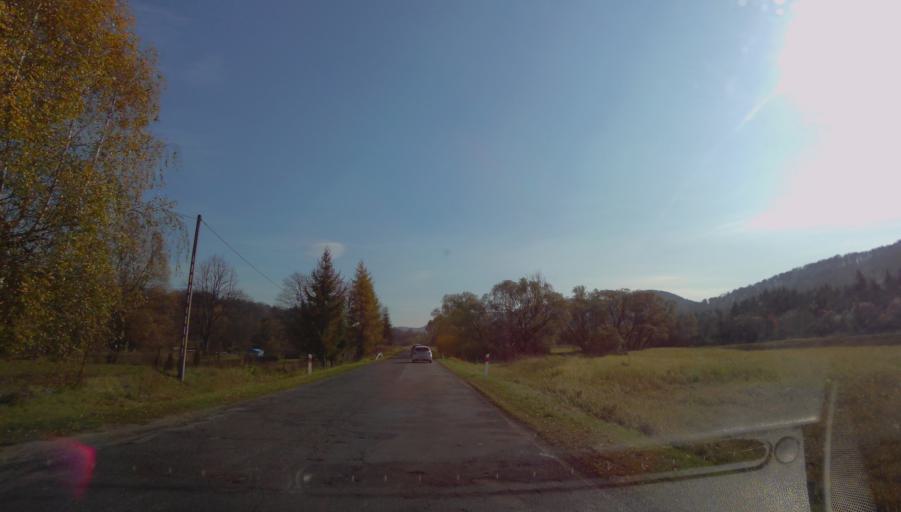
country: PL
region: Subcarpathian Voivodeship
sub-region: Powiat sanocki
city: Rzepedz
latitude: 49.2278
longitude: 22.1709
